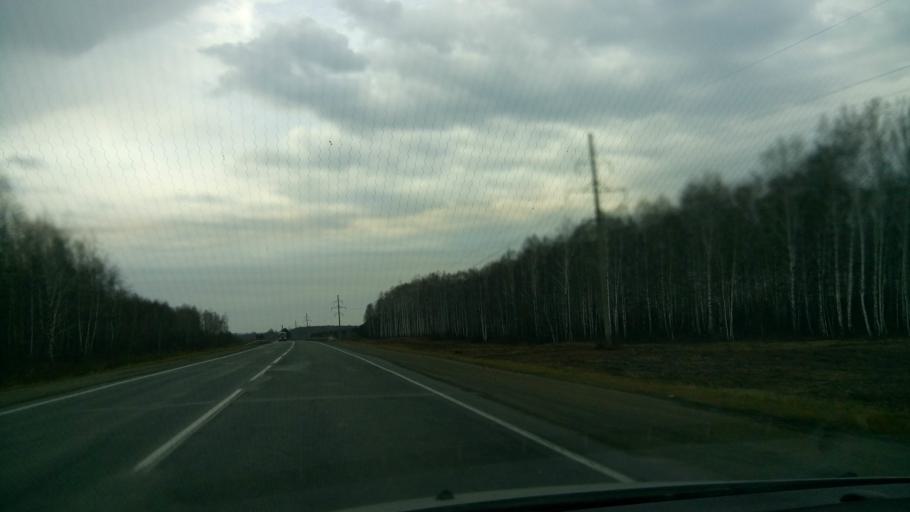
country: RU
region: Sverdlovsk
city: Obukhovskoye
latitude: 56.8592
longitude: 62.6235
